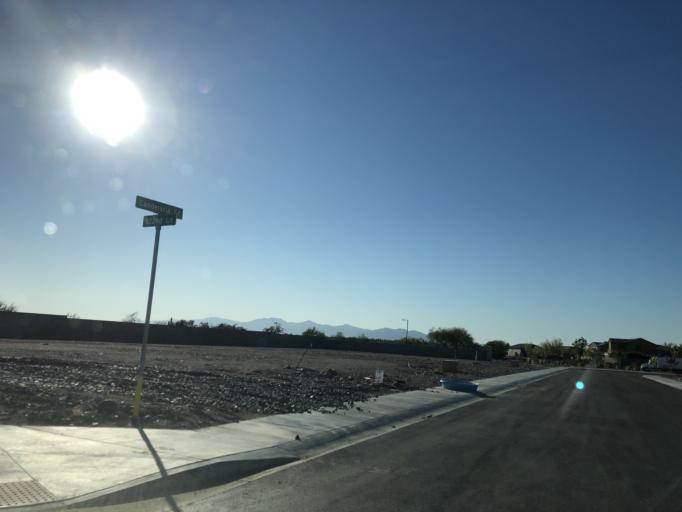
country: US
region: Arizona
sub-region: Maricopa County
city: Sun City West
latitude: 33.6900
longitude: -112.3235
